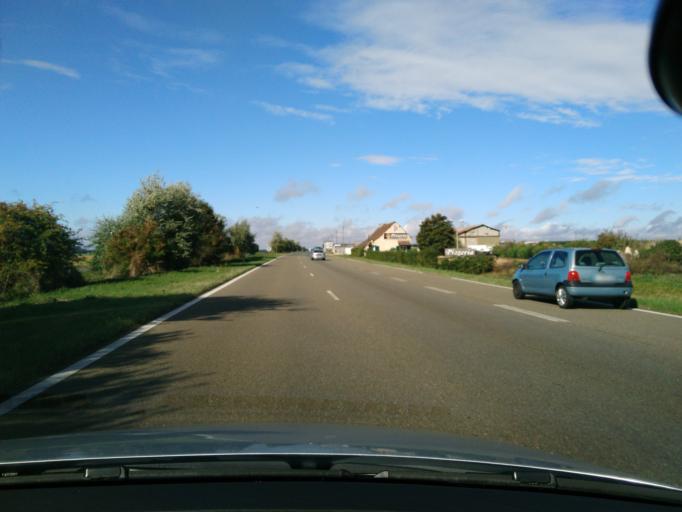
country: FR
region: Centre
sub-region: Departement d'Eure-et-Loir
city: Vert-en-Drouais
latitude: 48.7441
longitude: 1.2883
